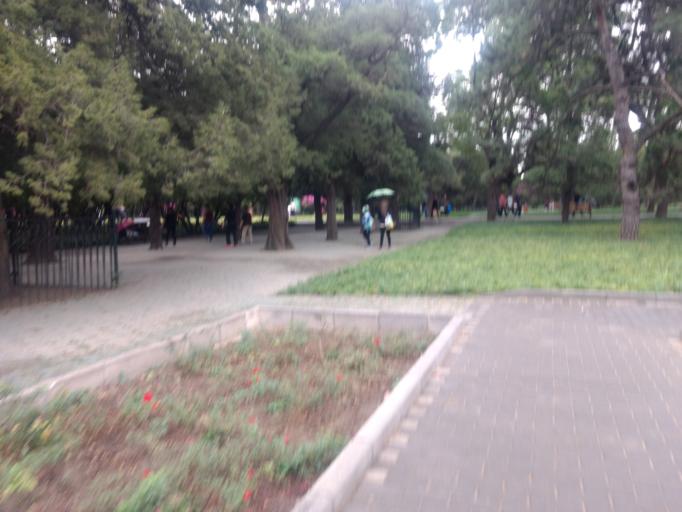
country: CN
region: Beijing
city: Longtan
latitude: 39.8804
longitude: 116.4038
